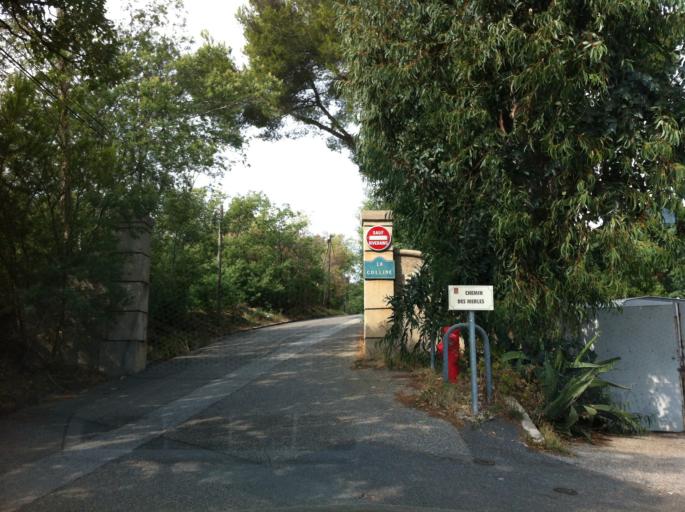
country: FR
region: Provence-Alpes-Cote d'Azur
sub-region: Departement du Var
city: Gassin
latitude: 43.2817
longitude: 6.5774
